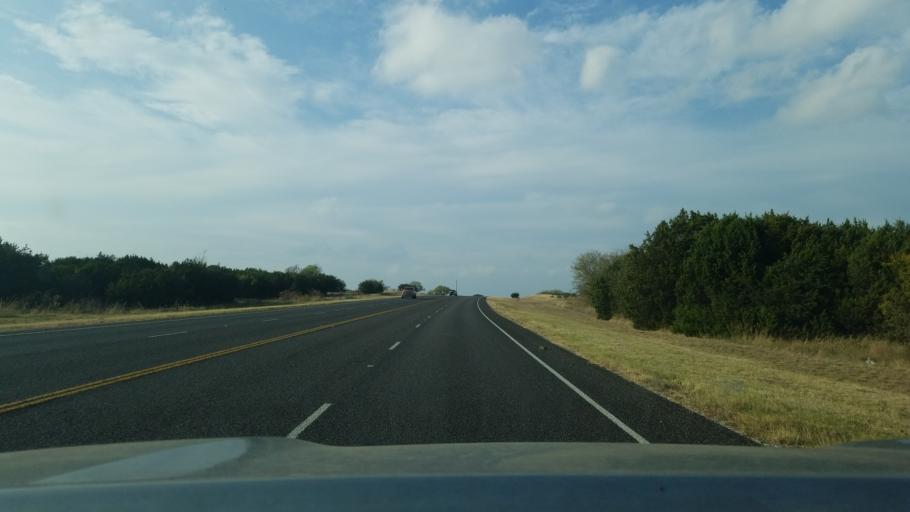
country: US
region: Texas
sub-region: Mills County
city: Goldthwaite
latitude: 31.2383
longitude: -98.4196
